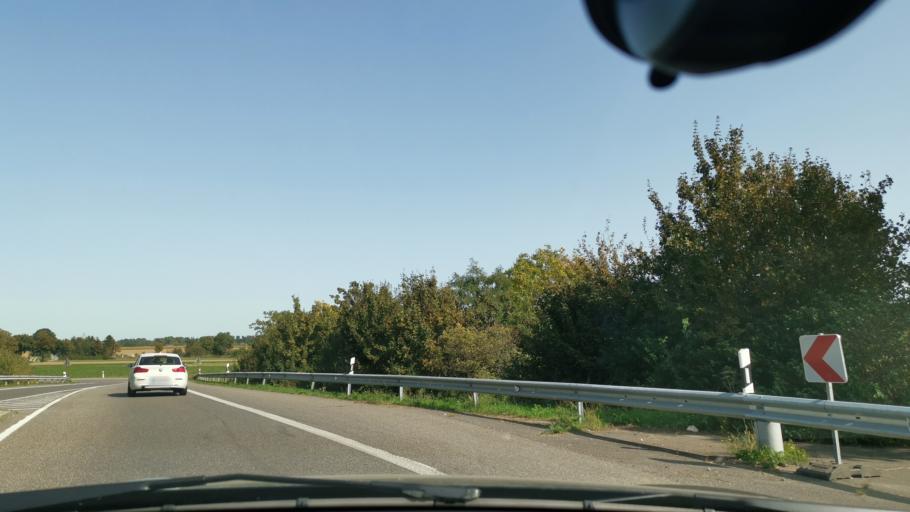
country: DE
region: North Rhine-Westphalia
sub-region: Regierungsbezirk Dusseldorf
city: Neubrueck
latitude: 51.1326
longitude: 6.6318
